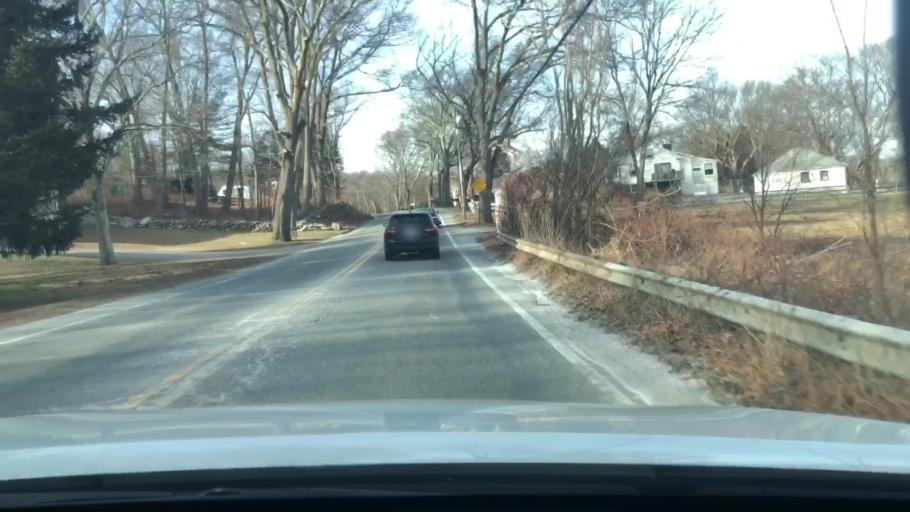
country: US
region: Massachusetts
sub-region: Worcester County
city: Grafton
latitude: 42.2029
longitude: -71.6618
